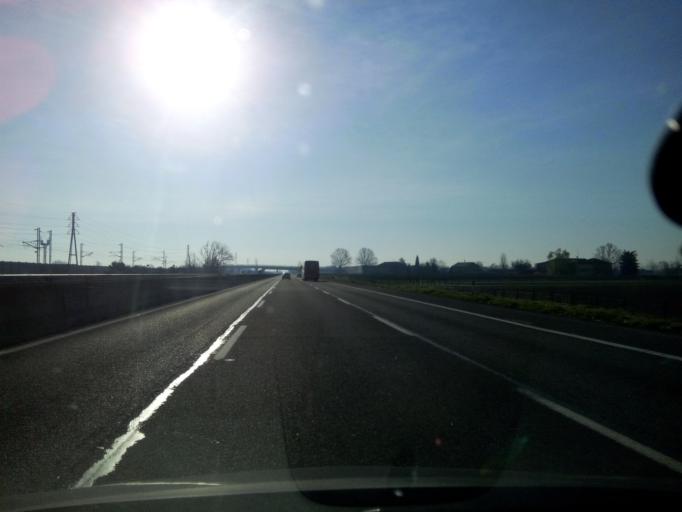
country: IT
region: Emilia-Romagna
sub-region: Provincia di Reggio Emilia
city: Rubiera
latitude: 44.6863
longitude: 10.7905
